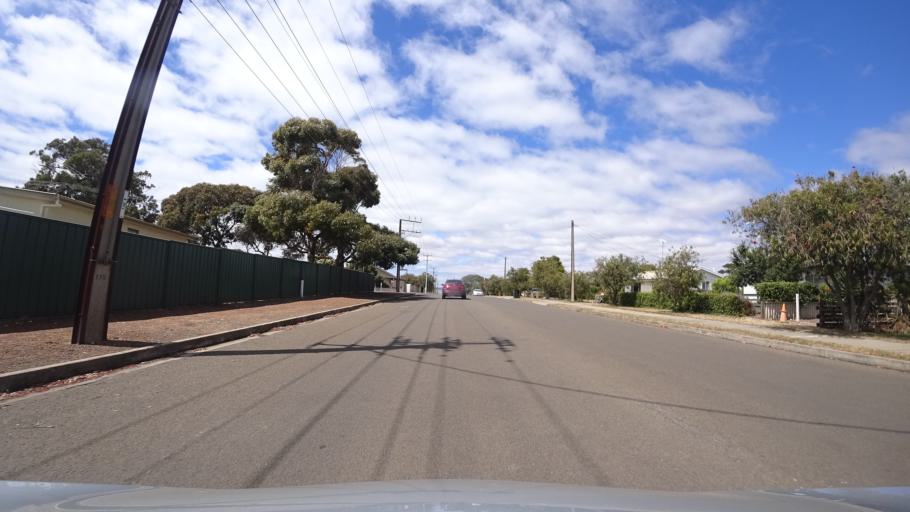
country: AU
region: South Australia
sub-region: Kangaroo Island
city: Kingscote
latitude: -35.6561
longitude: 137.6339
